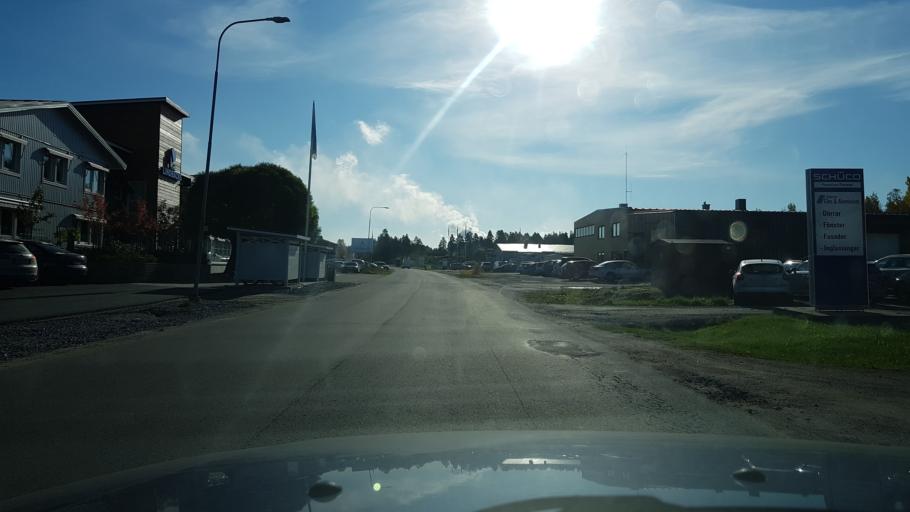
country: SE
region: Norrbotten
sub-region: Pitea Kommun
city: Bergsviken
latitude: 65.3379
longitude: 21.4127
